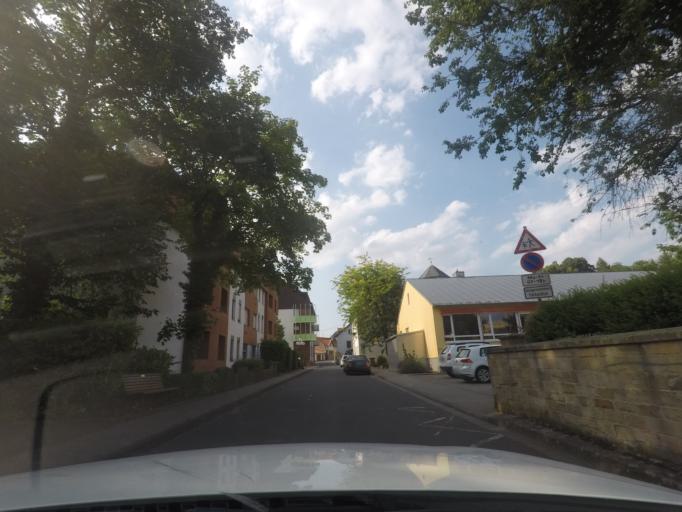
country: DE
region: Rheinland-Pfalz
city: Staudernheim
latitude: 49.7864
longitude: 7.6519
